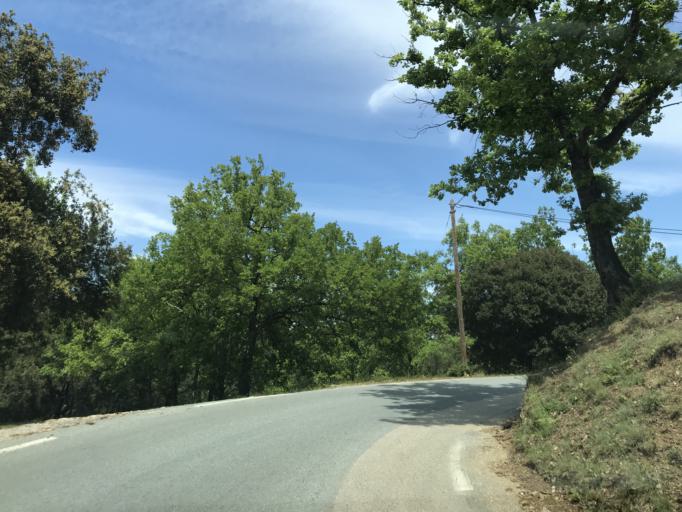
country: FR
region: Provence-Alpes-Cote d'Azur
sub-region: Departement du Var
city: Montauroux
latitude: 43.5870
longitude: 6.8180
